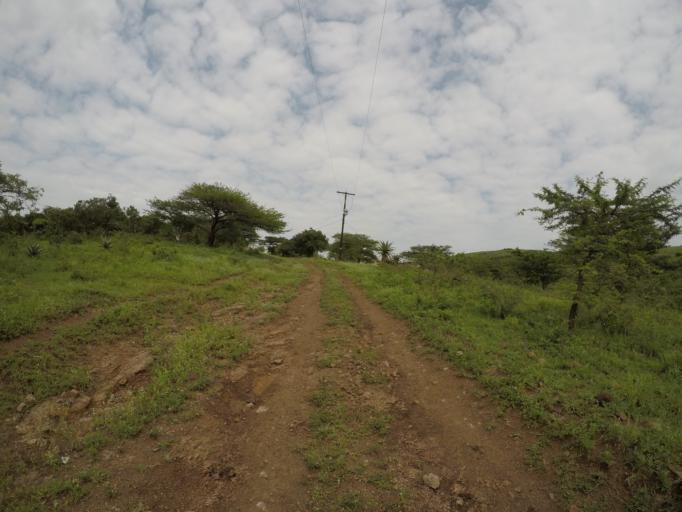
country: ZA
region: KwaZulu-Natal
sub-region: uThungulu District Municipality
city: Empangeni
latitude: -28.6261
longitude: 31.9110
